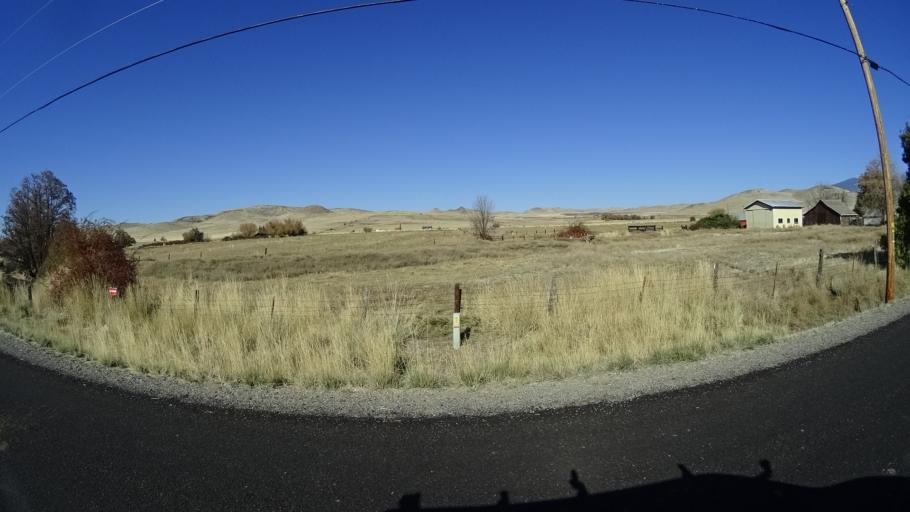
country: US
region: California
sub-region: Siskiyou County
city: Montague
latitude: 41.7263
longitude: -122.4072
